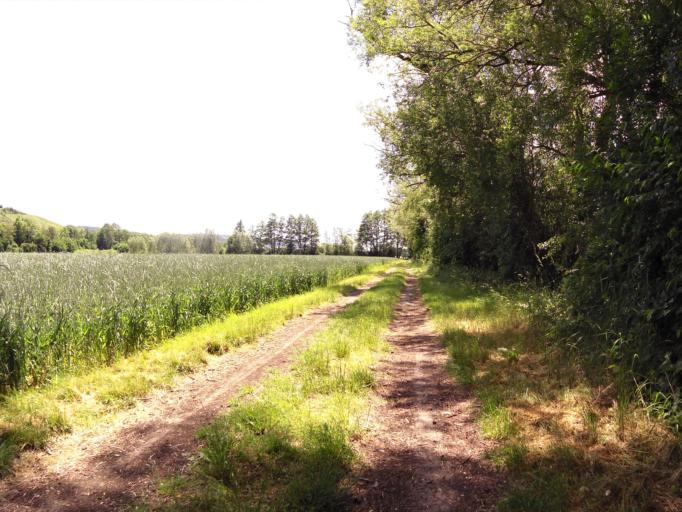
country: DE
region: Bavaria
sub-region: Regierungsbezirk Unterfranken
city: Zellingen
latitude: 49.8949
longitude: 9.8306
